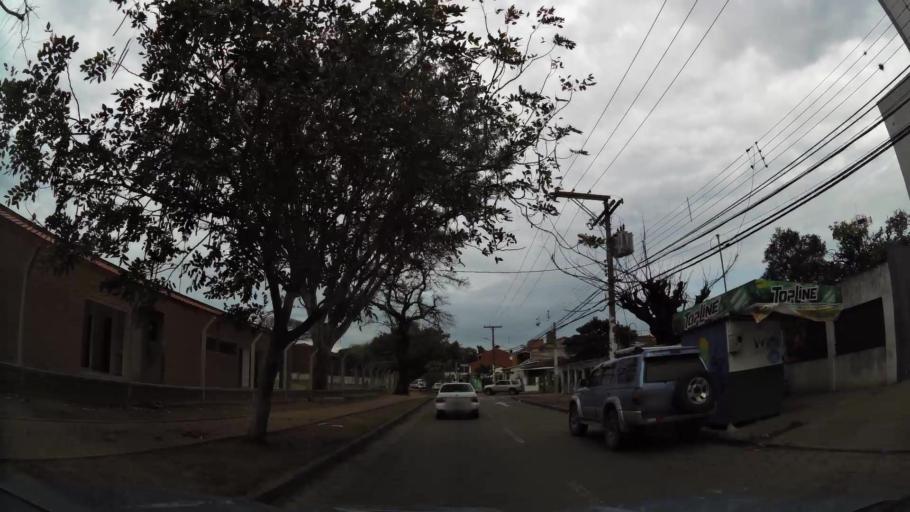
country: BO
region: Santa Cruz
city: Santa Cruz de la Sierra
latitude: -17.7735
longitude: -63.1715
